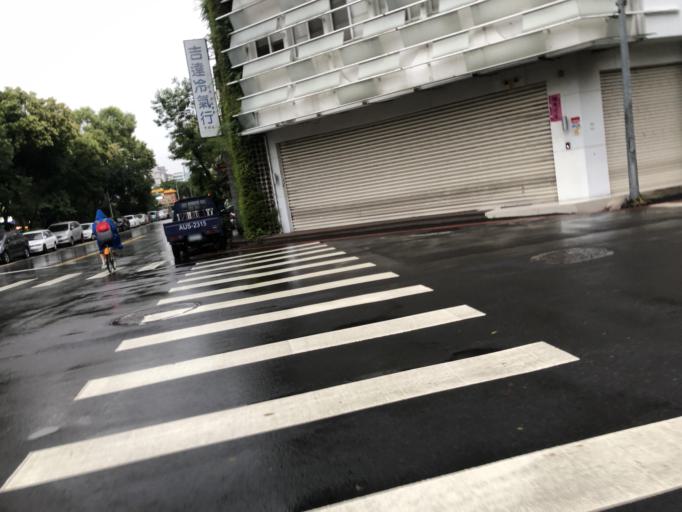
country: TW
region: Taiwan
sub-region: Taichung City
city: Taichung
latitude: 24.1616
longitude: 120.6767
